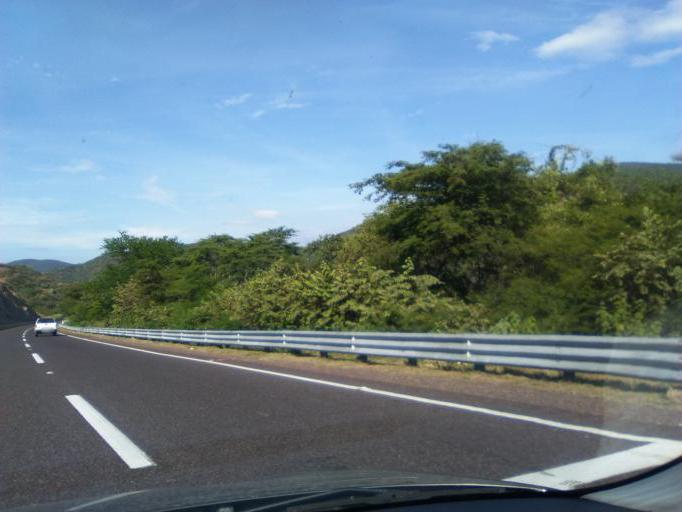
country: MX
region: Guerrero
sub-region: Huitzuco de los Figueroa
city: Ciudad de Huitzuco
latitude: 18.3459
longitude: -99.1880
